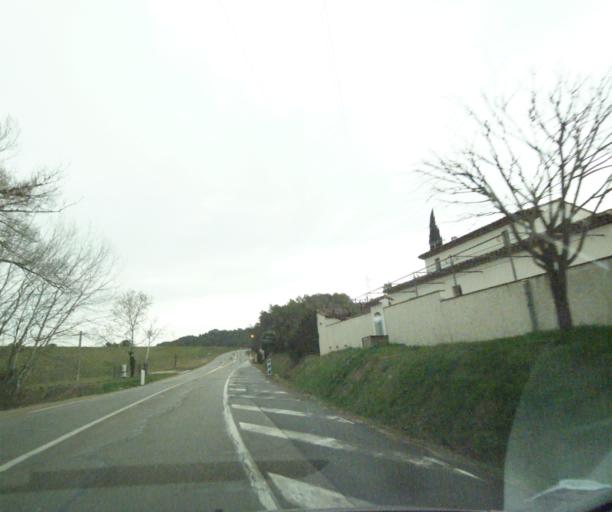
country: FR
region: Provence-Alpes-Cote d'Azur
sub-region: Departement des Bouches-du-Rhone
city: Le Puy-Sainte-Reparade
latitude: 43.6591
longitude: 5.4185
